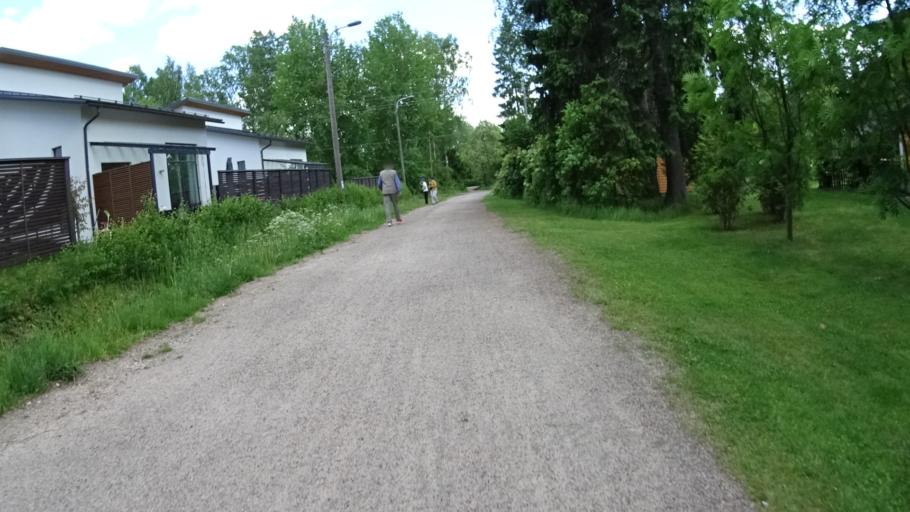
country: FI
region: Uusimaa
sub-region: Helsinki
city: Otaniemi
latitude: 60.1943
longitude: 24.8014
